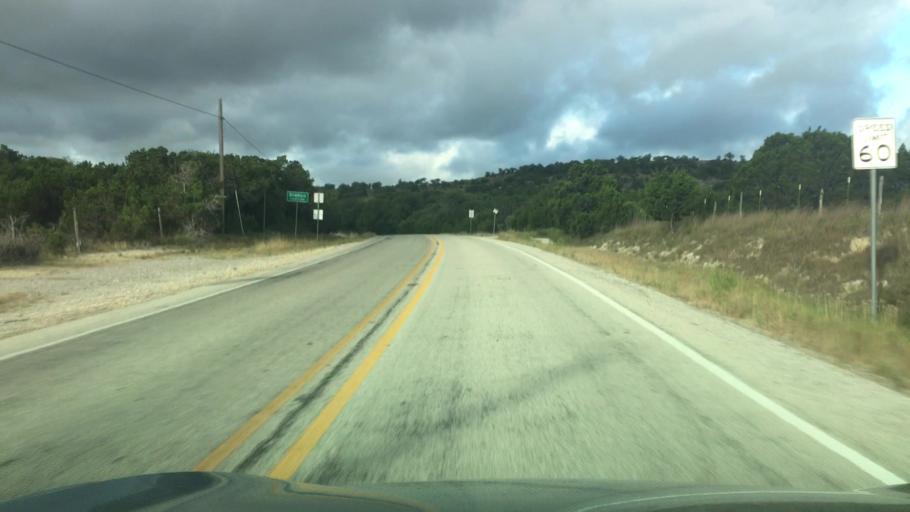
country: US
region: Texas
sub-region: Hays County
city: Dripping Springs
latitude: 30.1553
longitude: -98.2516
